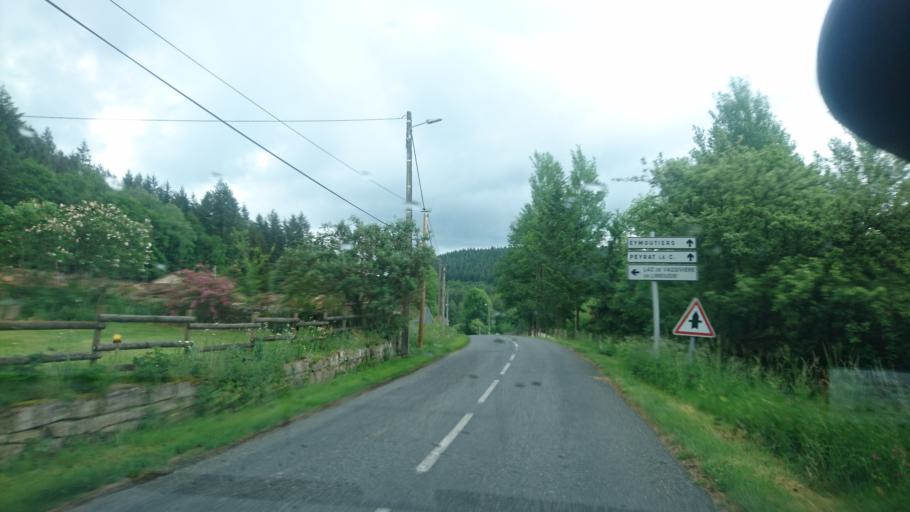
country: FR
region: Limousin
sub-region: Departement de la Haute-Vienne
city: Peyrat-le-Chateau
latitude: 45.8106
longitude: 1.8217
